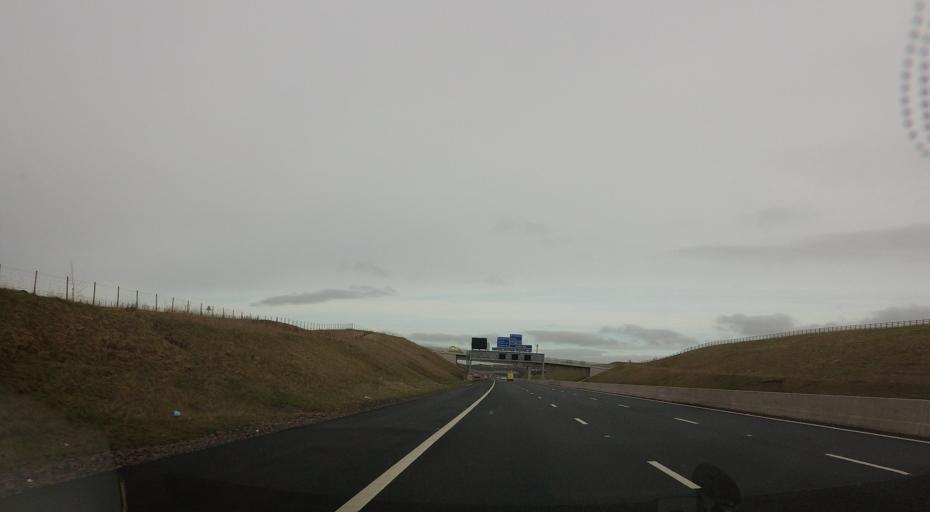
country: GB
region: Scotland
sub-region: North Lanarkshire
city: Coatbridge
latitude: 55.8420
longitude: -4.0470
